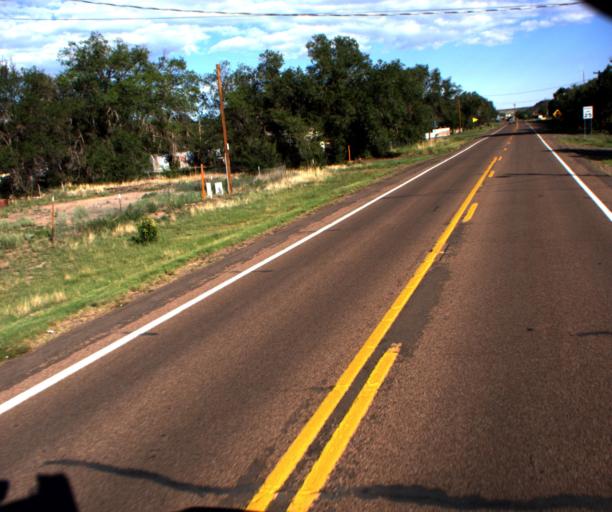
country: US
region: Arizona
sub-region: Apache County
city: Springerville
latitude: 34.1302
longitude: -109.2678
